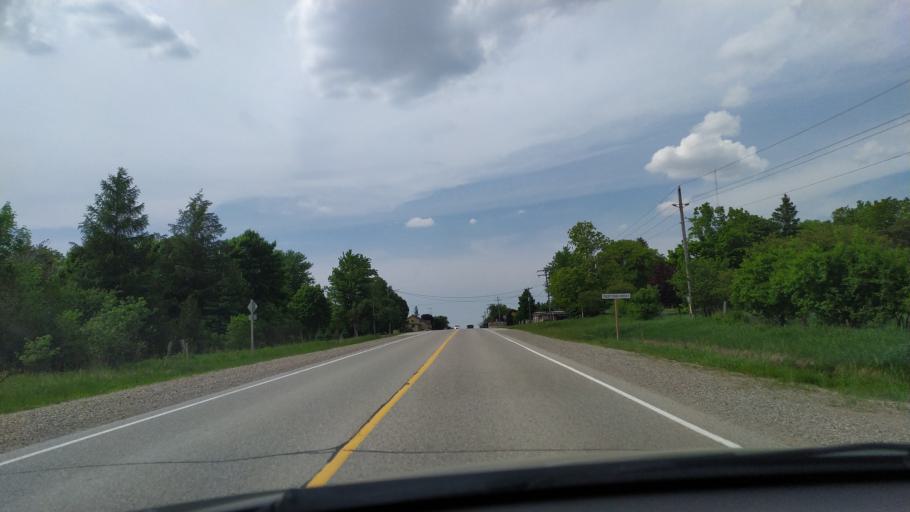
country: CA
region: Ontario
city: Stratford
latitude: 43.2154
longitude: -81.0686
